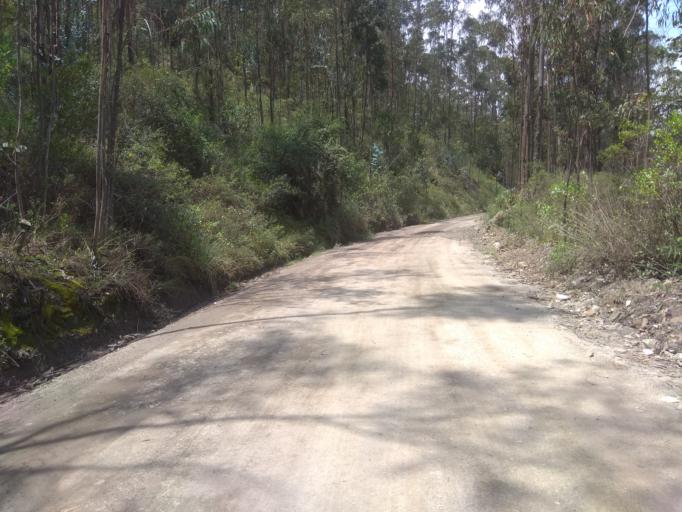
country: CO
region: Boyaca
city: Socha Viejo
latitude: 5.9803
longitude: -72.7342
